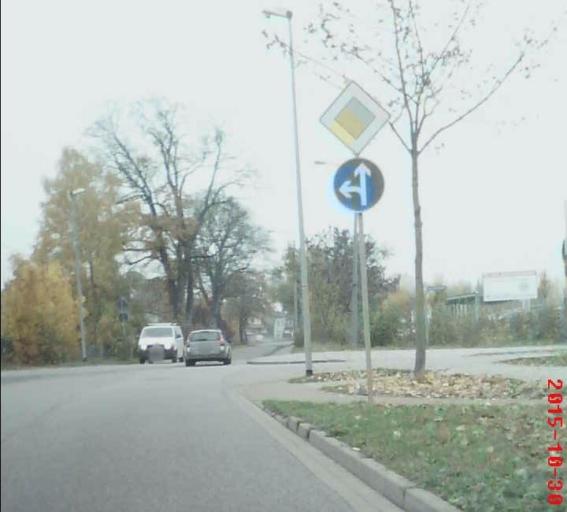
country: DE
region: Thuringia
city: Muehlhausen
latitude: 51.2180
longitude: 10.4441
